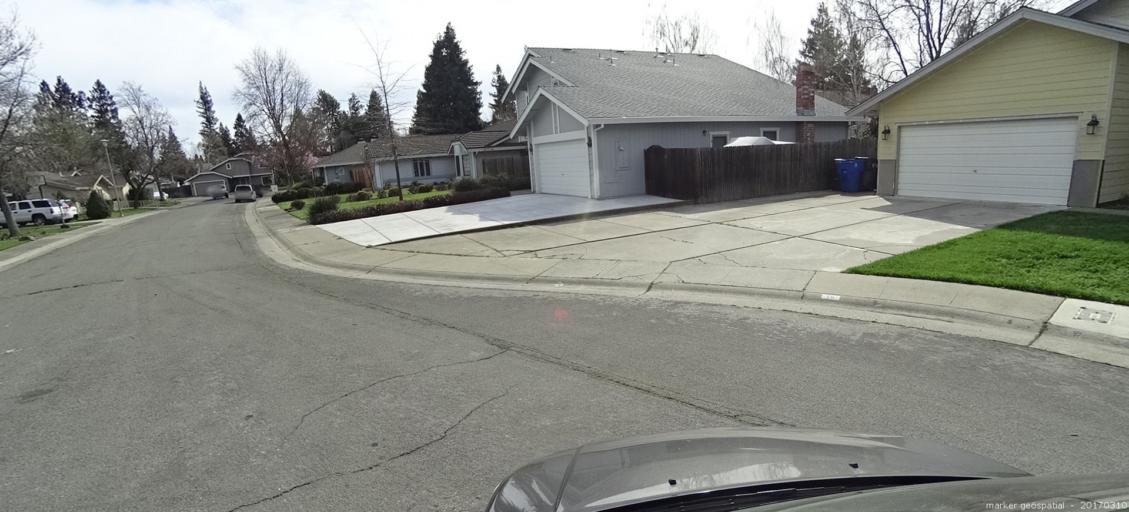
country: US
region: California
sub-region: Sacramento County
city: Parkway
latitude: 38.4919
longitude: -121.5306
